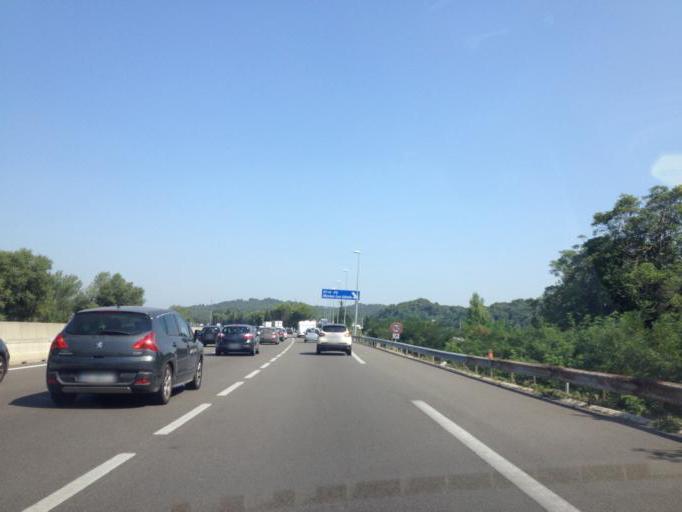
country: FR
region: Provence-Alpes-Cote d'Azur
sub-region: Departement du Vaucluse
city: Mornas
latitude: 44.2115
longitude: 4.7241
